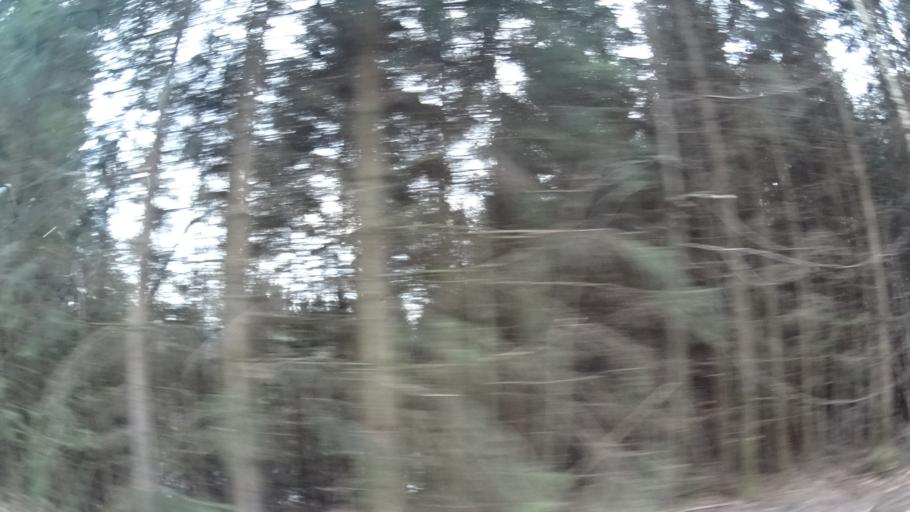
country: DE
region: Rheinland-Pfalz
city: Hattgenstein
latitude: 49.7166
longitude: 7.1420
